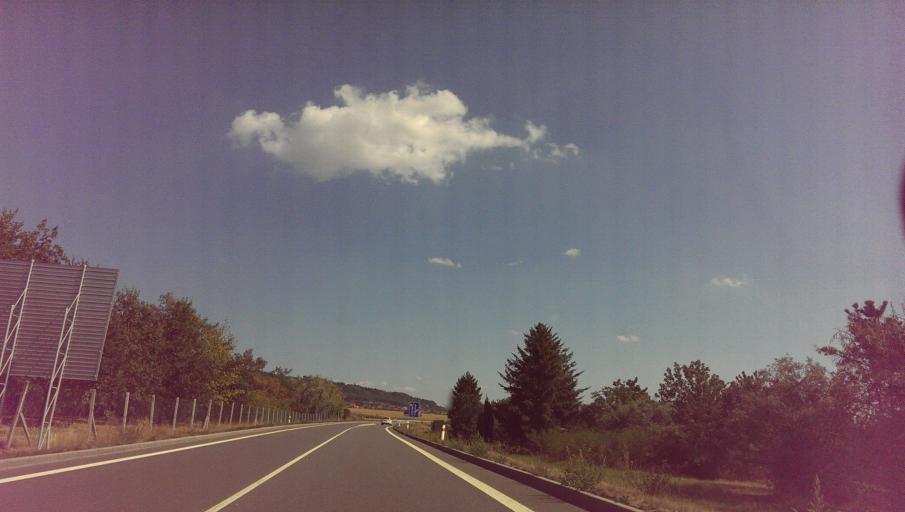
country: CZ
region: Zlin
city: Holesov
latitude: 49.3339
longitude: 17.5923
